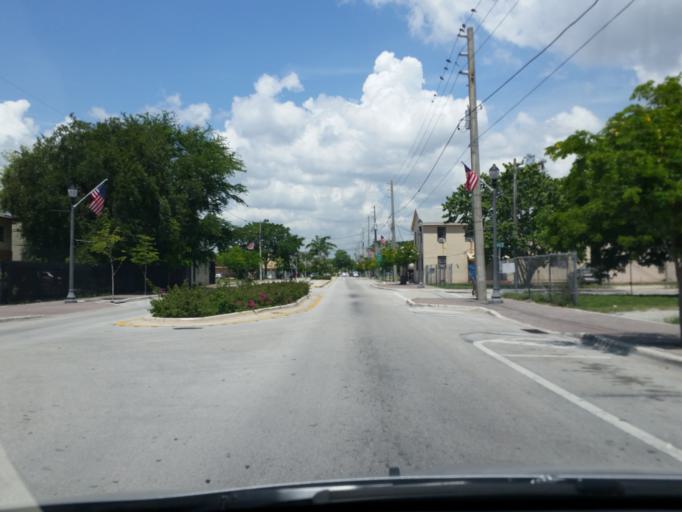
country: US
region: Florida
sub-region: Miami-Dade County
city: Coconut Grove
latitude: 25.7279
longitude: -80.2494
